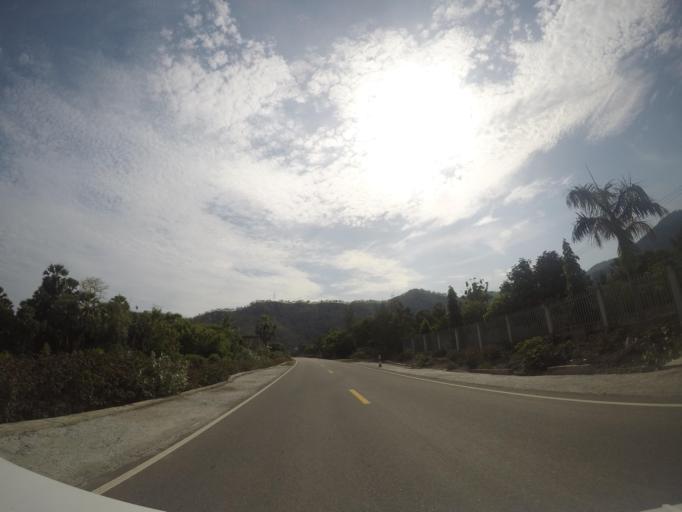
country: ID
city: Metinaro
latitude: -8.5374
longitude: 125.7041
